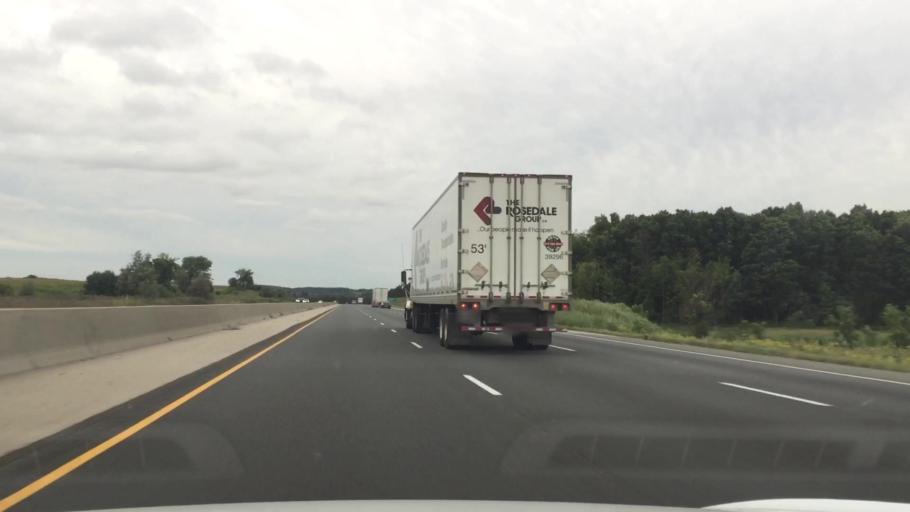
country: CA
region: Ontario
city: Kitchener
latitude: 43.3235
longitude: -80.4595
